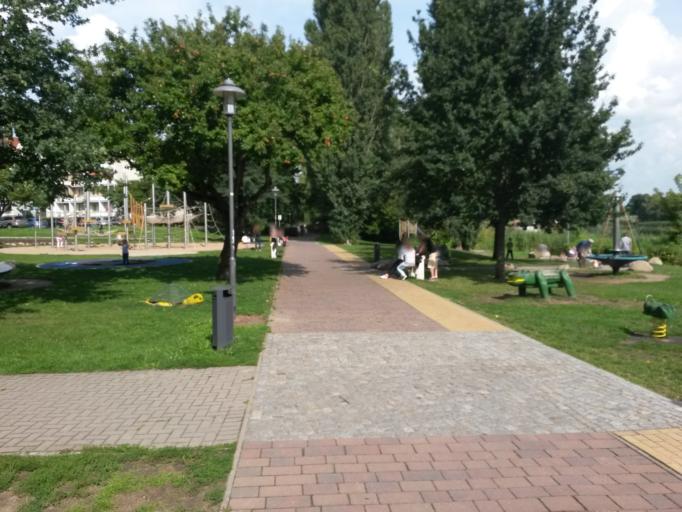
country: DE
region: Brandenburg
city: Schwedt (Oder)
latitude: 53.0514
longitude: 14.2829
